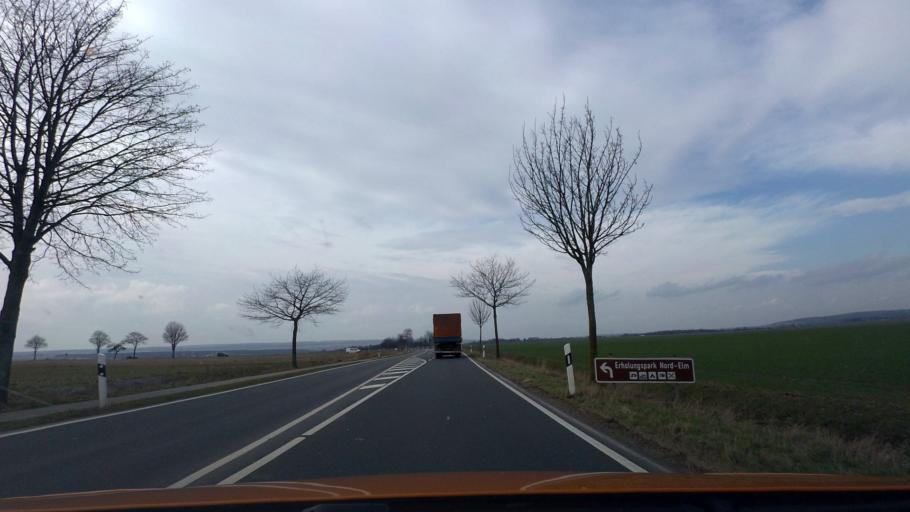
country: DE
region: Lower Saxony
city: Frellstedt
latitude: 52.2243
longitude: 10.9402
